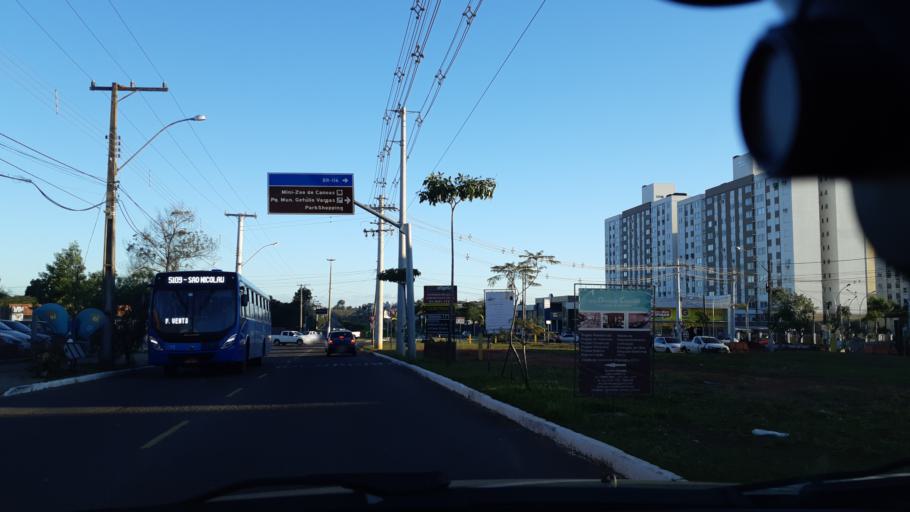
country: BR
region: Rio Grande do Sul
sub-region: Canoas
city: Canoas
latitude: -29.9176
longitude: -51.1546
